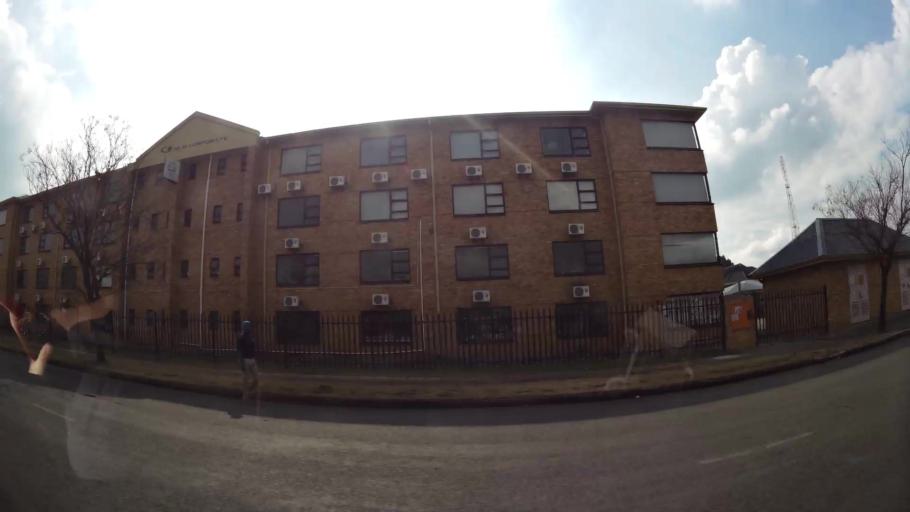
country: ZA
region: Gauteng
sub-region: Sedibeng District Municipality
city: Vereeniging
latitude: -26.6713
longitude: 27.9263
